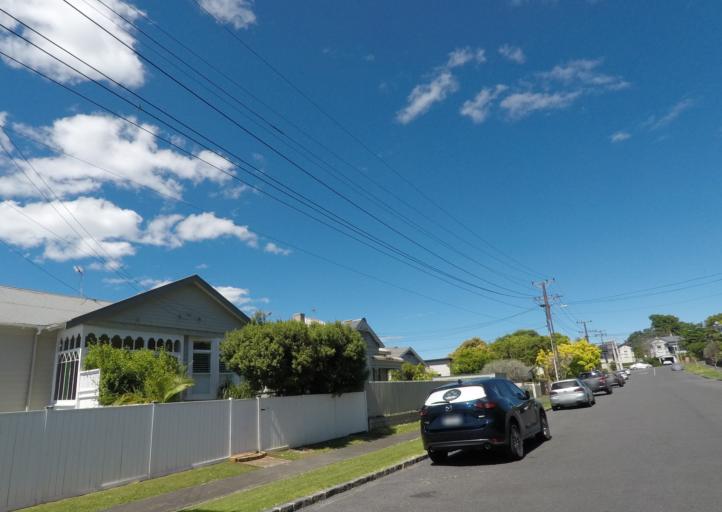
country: NZ
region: Auckland
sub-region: Auckland
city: Auckland
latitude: -36.8712
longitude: 174.7319
